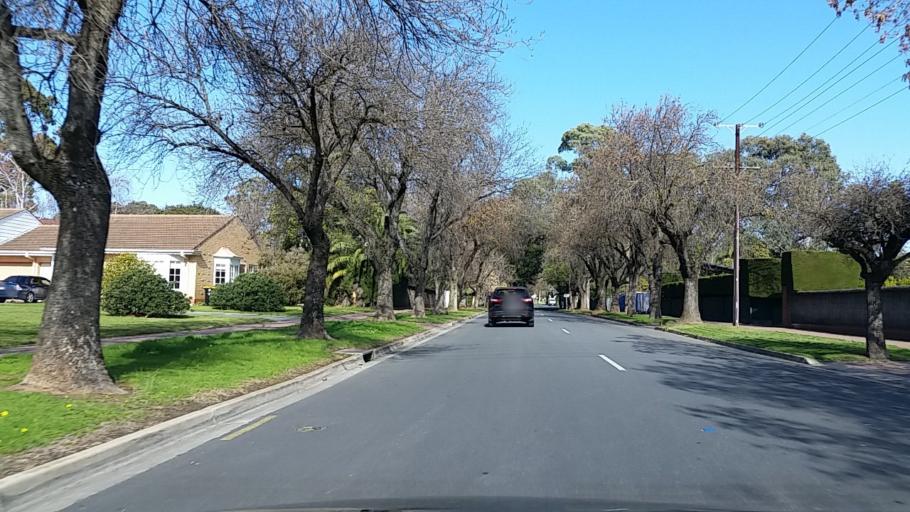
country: AU
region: South Australia
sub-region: Burnside
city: Tusmore
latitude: -34.9336
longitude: 138.6516
